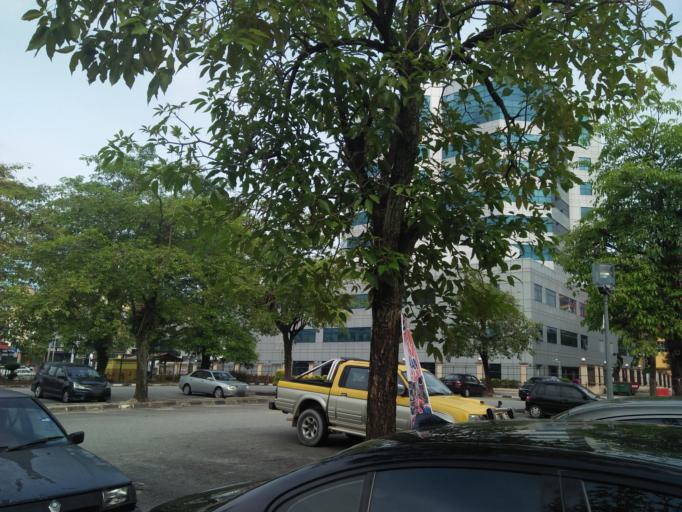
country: MY
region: Perak
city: Ipoh
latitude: 4.6027
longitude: 101.0947
